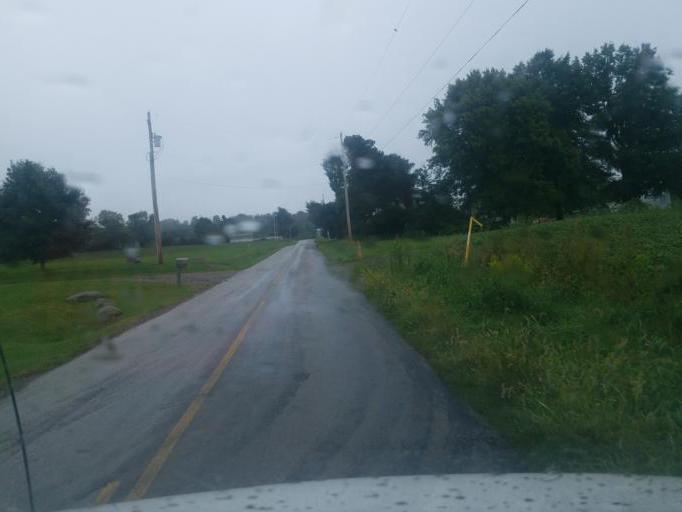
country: US
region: Ohio
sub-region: Medina County
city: Seville
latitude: 40.9824
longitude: -81.8442
